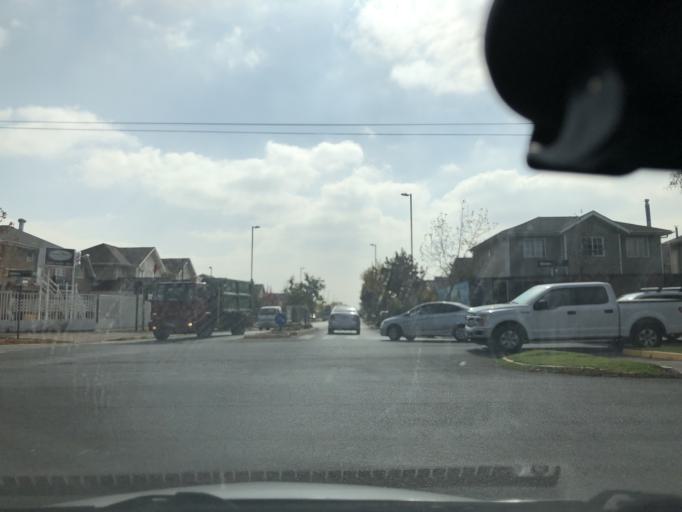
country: CL
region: Santiago Metropolitan
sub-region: Provincia de Cordillera
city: Puente Alto
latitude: -33.5993
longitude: -70.5841
